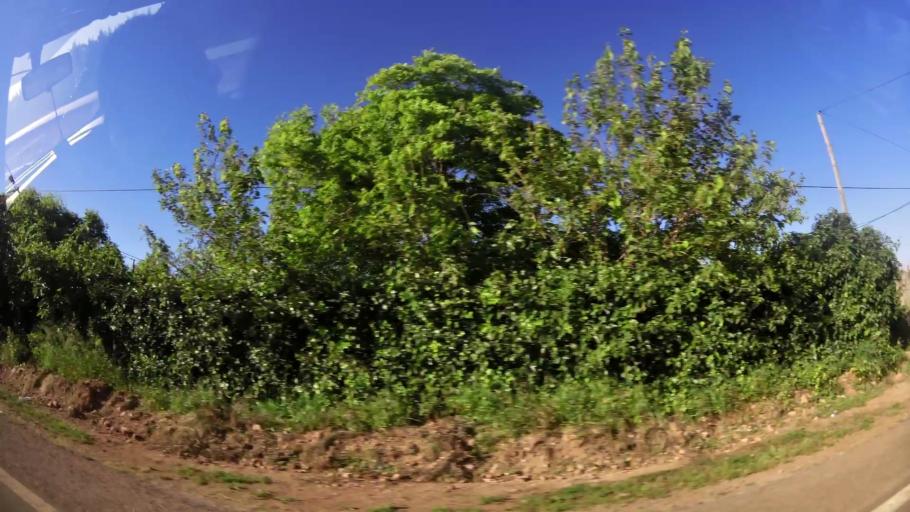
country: MA
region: Oriental
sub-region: Berkane-Taourirt
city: Ahfir
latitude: 35.0047
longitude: -2.1835
